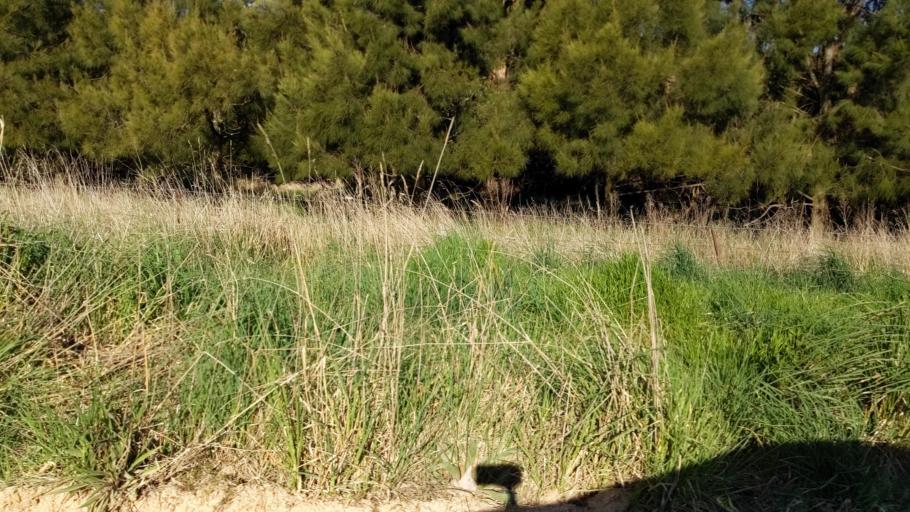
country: AU
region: New South Wales
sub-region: Blayney
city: Millthorpe
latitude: -33.4049
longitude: 149.3076
